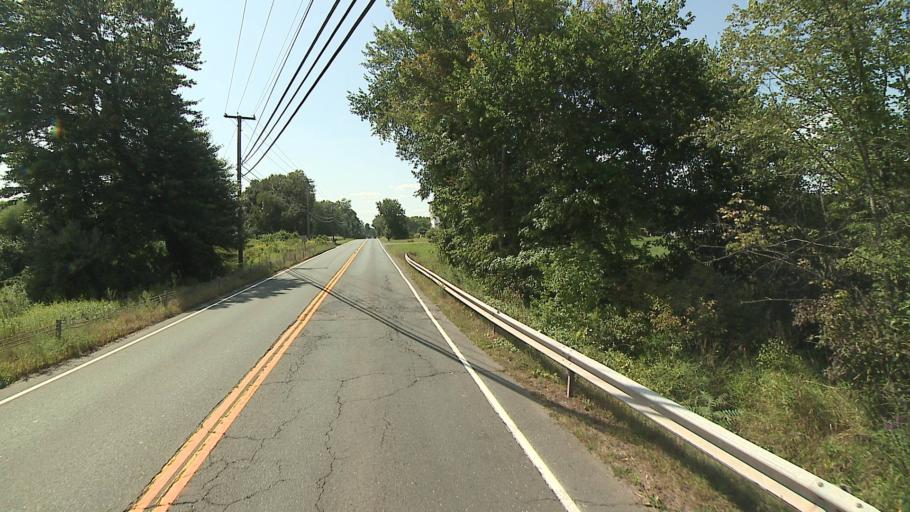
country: US
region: Connecticut
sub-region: Hartford County
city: Southwood Acres
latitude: 41.9351
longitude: -72.5809
